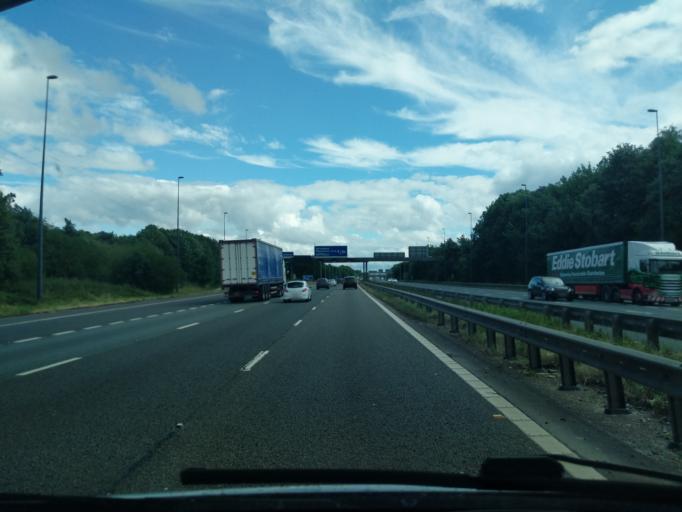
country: GB
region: England
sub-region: Warrington
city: Croft
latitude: 53.4259
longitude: -2.5559
